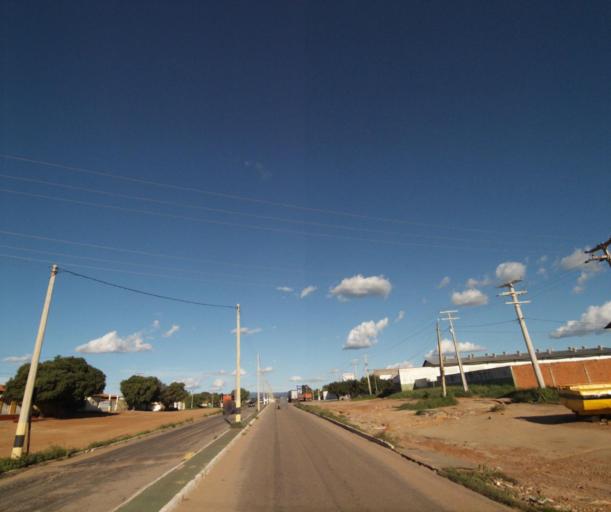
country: BR
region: Bahia
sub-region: Guanambi
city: Guanambi
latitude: -14.2104
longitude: -42.7862
